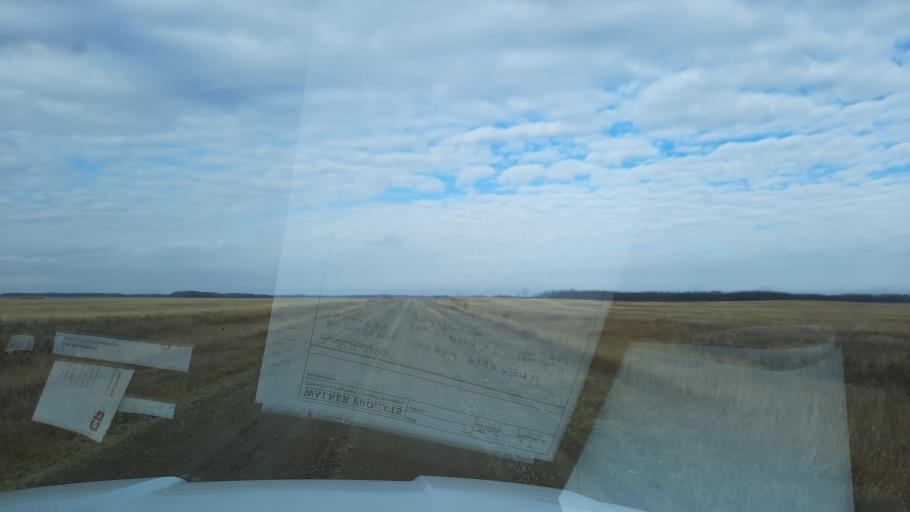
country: CA
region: Saskatchewan
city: Pilot Butte
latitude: 50.7475
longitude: -104.2020
